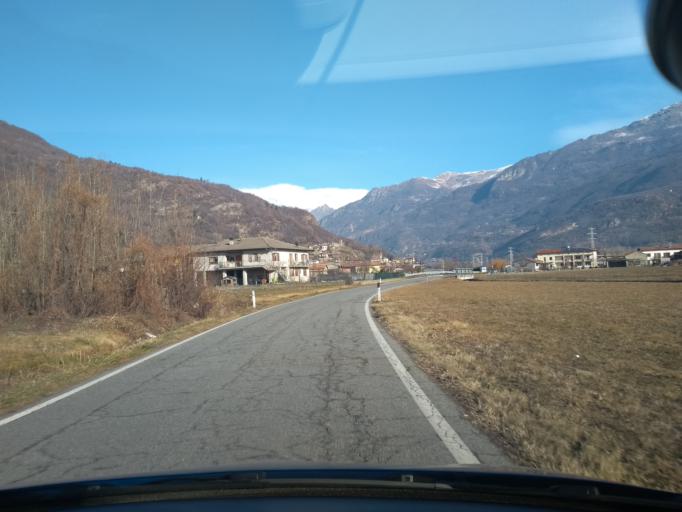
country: IT
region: Piedmont
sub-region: Provincia di Torino
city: Quassolo
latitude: 45.5166
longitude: 7.8328
